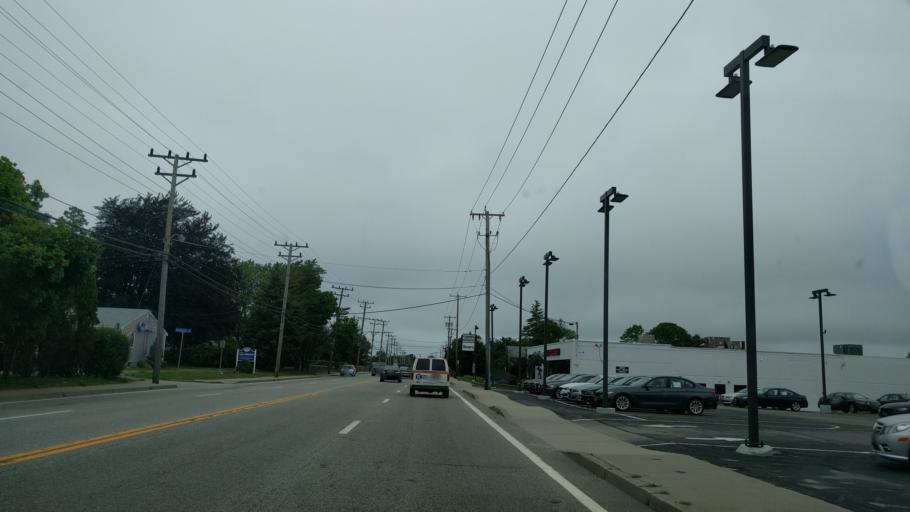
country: US
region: Rhode Island
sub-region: Newport County
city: Middletown
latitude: 41.5321
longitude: -71.2934
